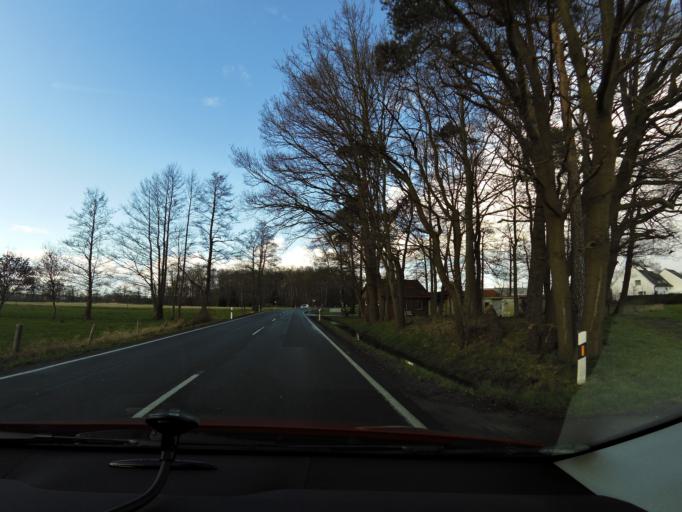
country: DE
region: North Rhine-Westphalia
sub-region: Regierungsbezirk Detmold
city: Verl
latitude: 51.8703
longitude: 8.4526
